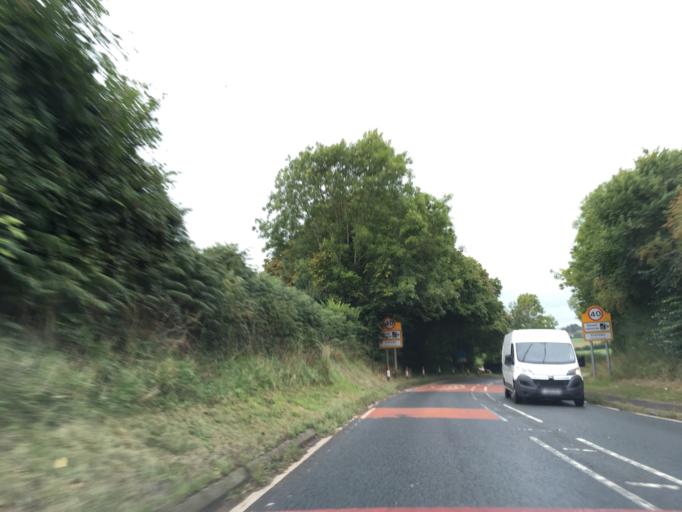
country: GB
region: England
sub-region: Herefordshire
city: Lea
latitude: 51.8984
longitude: -2.5216
